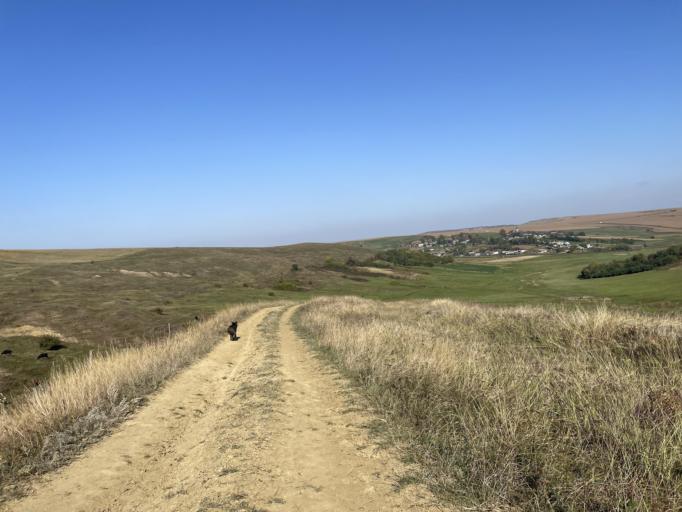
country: RO
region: Iasi
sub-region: Comuna Dumesti
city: Pausesti
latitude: 47.1531
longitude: 27.3095
